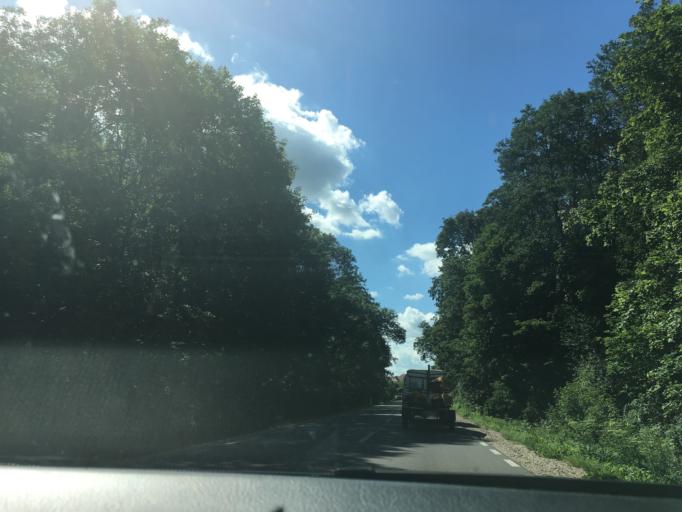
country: PL
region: Podlasie
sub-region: Powiat augustowski
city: Augustow
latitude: 53.8470
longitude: 23.0073
